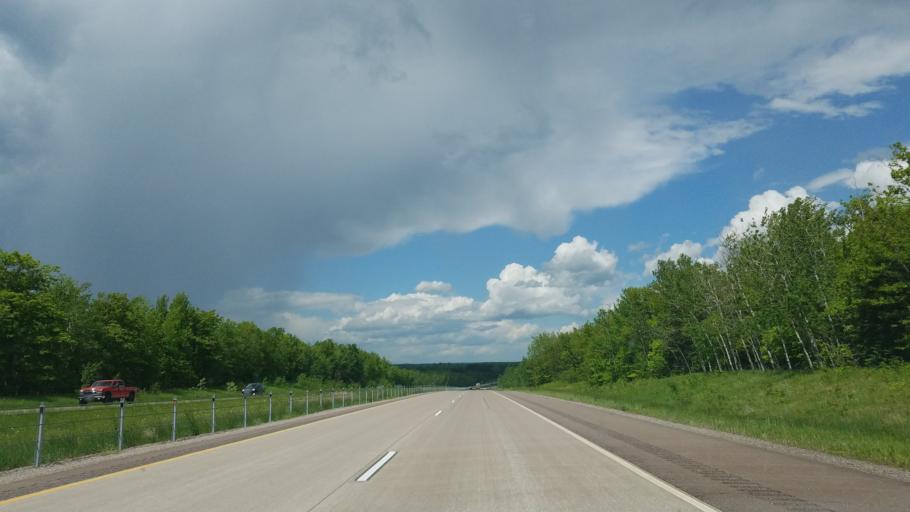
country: US
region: Minnesota
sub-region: Carlton County
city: Moose Lake
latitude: 46.4696
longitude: -92.7174
